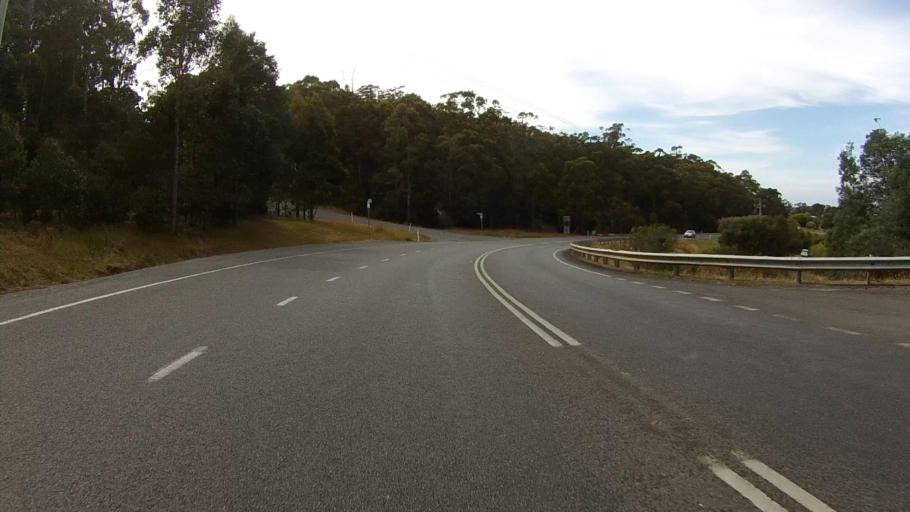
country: AU
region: Tasmania
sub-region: Kingborough
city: Kettering
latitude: -43.1128
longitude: 147.2436
